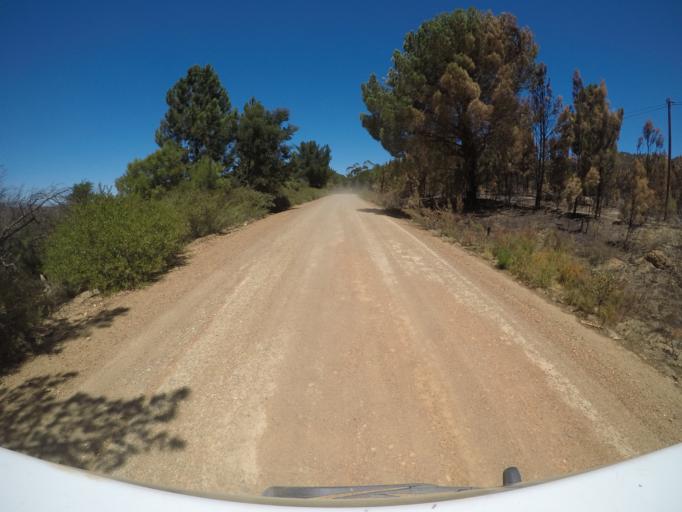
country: ZA
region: Western Cape
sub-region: Overberg District Municipality
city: Grabouw
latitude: -34.1618
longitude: 19.2251
